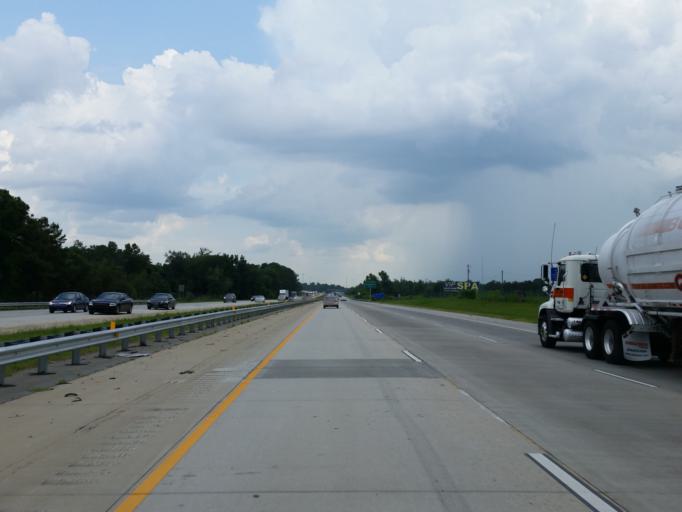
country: US
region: Georgia
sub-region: Dooly County
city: Unadilla
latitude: 32.2045
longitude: -83.7466
